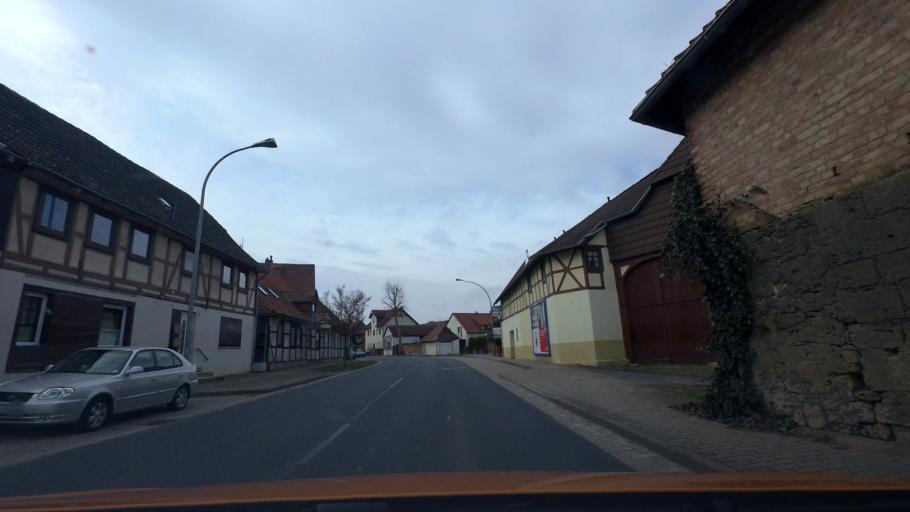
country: DE
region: Lower Saxony
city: Supplingen
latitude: 52.2280
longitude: 10.9020
